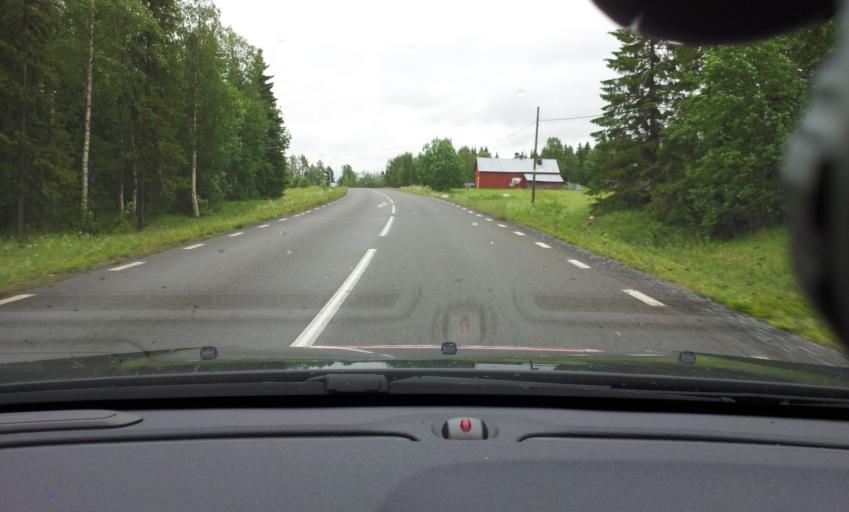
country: SE
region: Jaemtland
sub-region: OEstersunds Kommun
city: Lit
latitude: 63.6820
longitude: 15.0319
